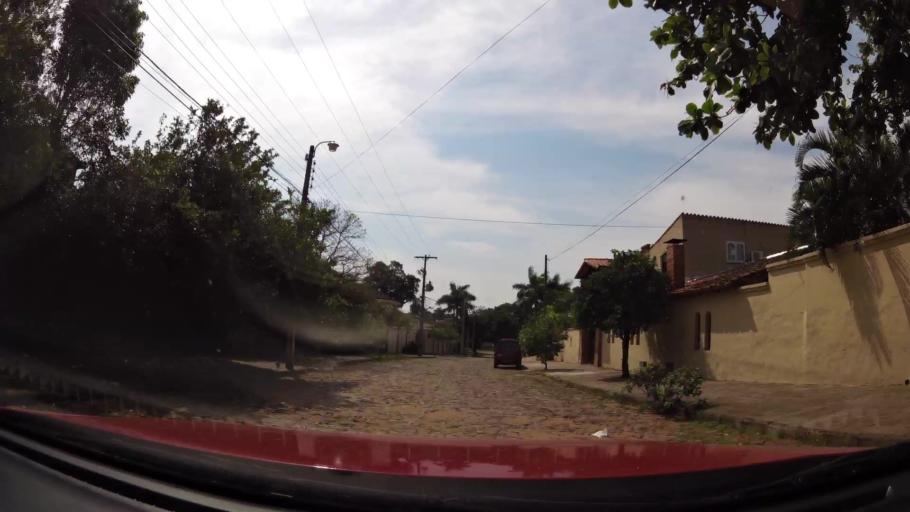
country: PY
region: Asuncion
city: Asuncion
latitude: -25.2666
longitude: -57.5650
